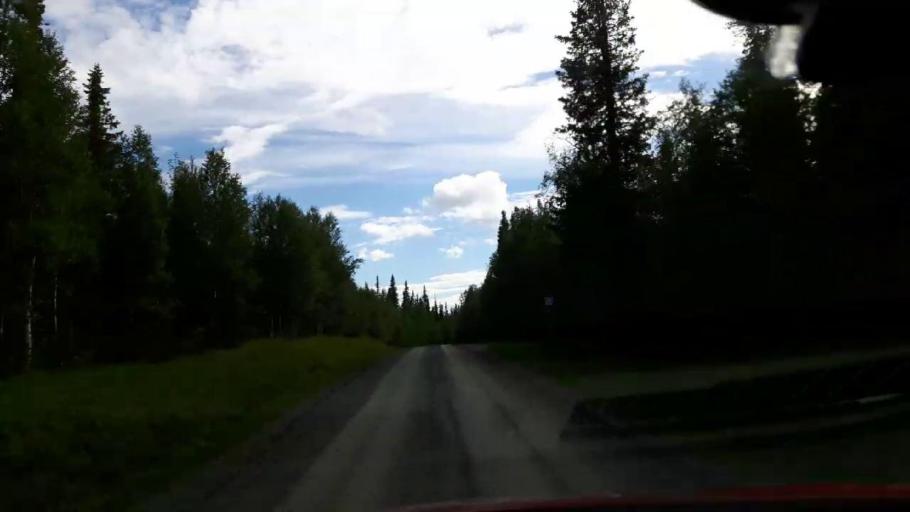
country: SE
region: Jaemtland
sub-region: Krokoms Kommun
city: Valla
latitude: 63.8669
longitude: 14.1162
